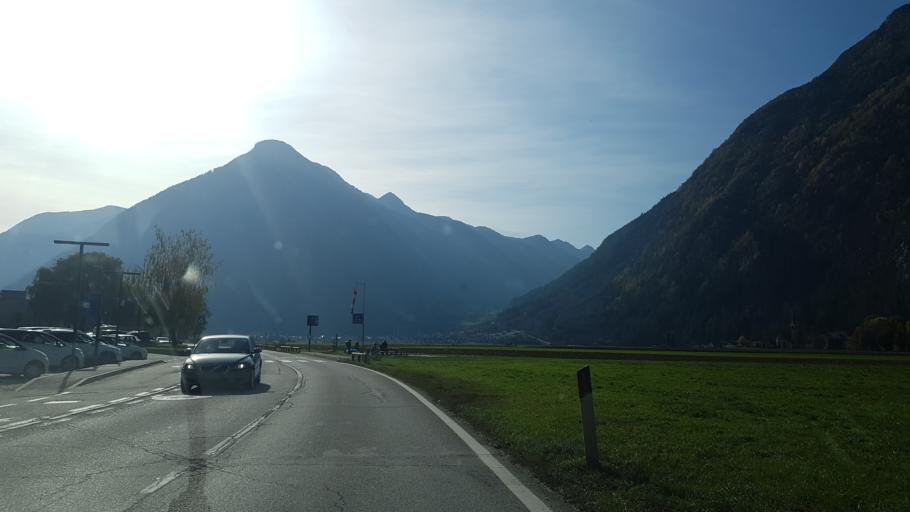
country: IT
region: Trentino-Alto Adige
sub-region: Bolzano
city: Campo Tures
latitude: 46.9123
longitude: 11.9621
